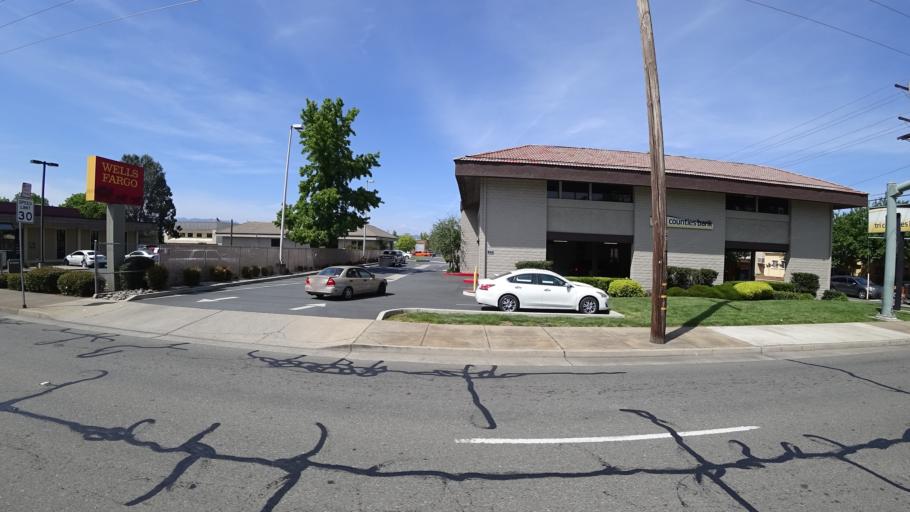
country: US
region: California
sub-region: Shasta County
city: Redding
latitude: 40.5711
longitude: -122.3558
